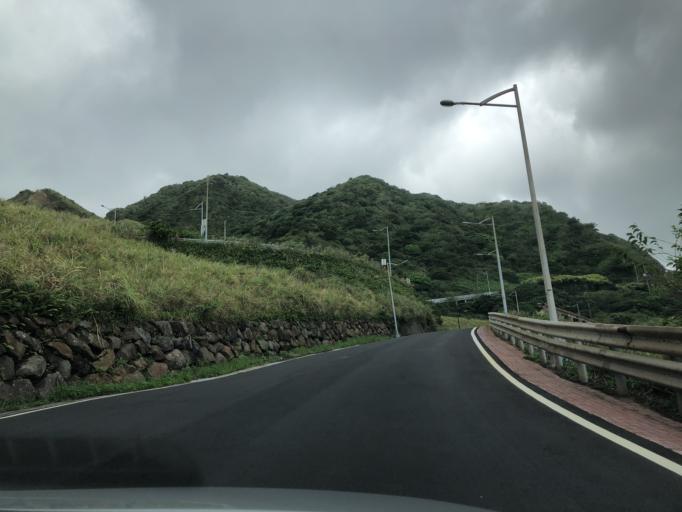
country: TW
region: Taiwan
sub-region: Keelung
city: Keelung
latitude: 25.1188
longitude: 121.8619
